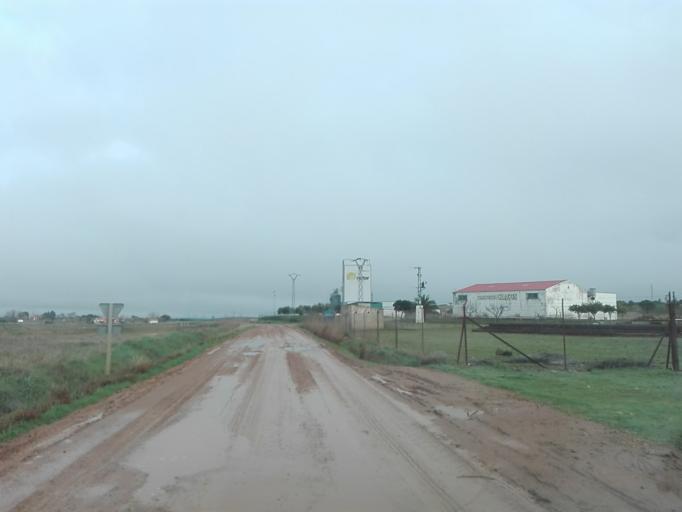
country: ES
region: Extremadura
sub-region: Provincia de Badajoz
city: Llerena
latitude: 38.2547
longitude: -6.0288
